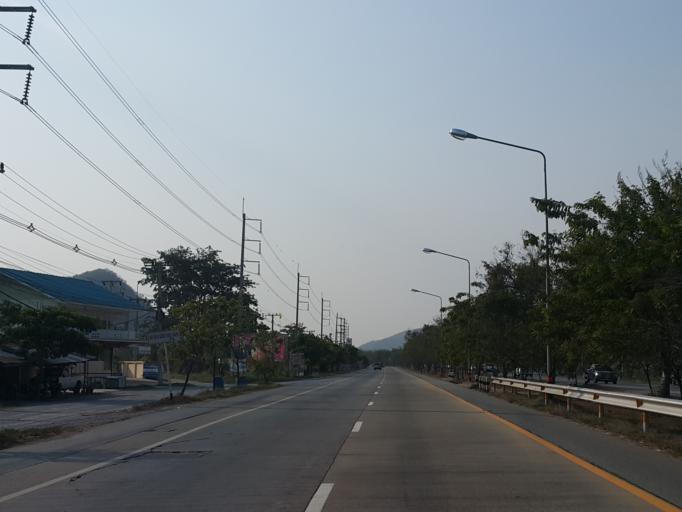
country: TH
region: Suphan Buri
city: Doembang Nangbuat
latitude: 14.8316
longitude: 100.1132
